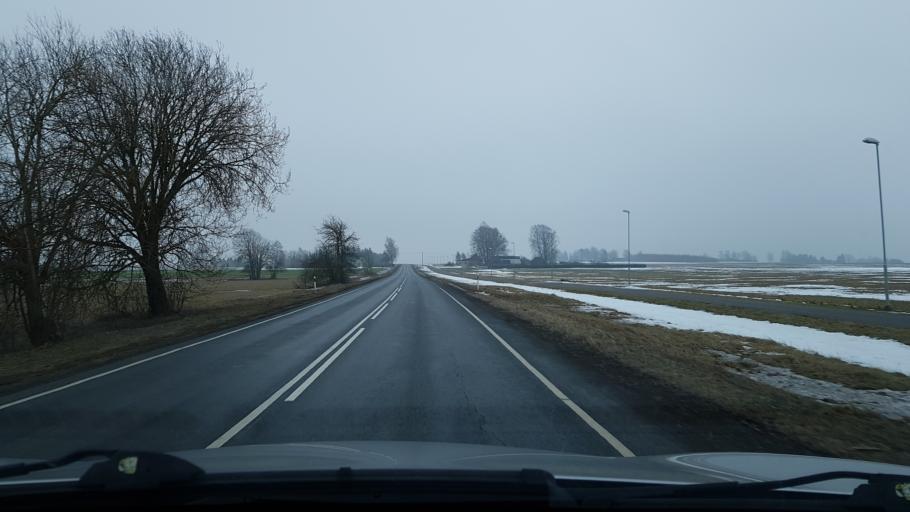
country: EE
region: Valgamaa
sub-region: Torva linn
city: Torva
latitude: 58.2254
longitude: 25.8890
